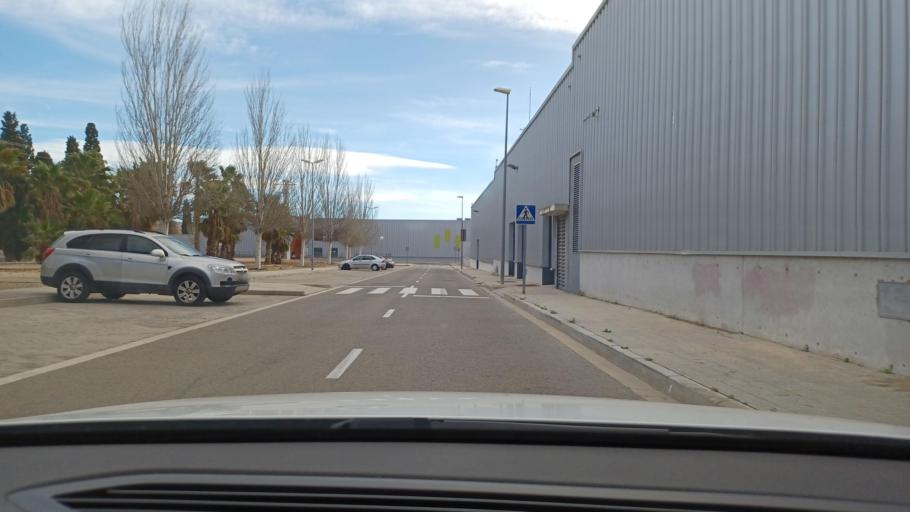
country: ES
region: Catalonia
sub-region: Provincia de Tarragona
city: Amposta
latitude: 40.7090
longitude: 0.5693
